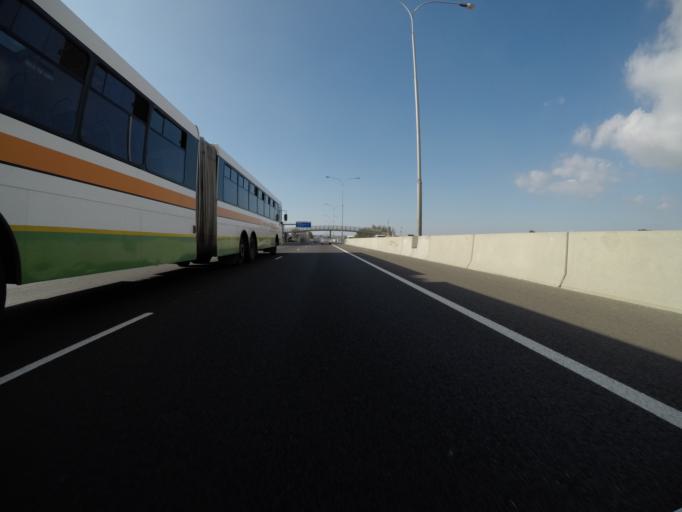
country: ZA
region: Western Cape
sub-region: City of Cape Town
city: Kraaifontein
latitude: -33.9289
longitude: 18.6628
